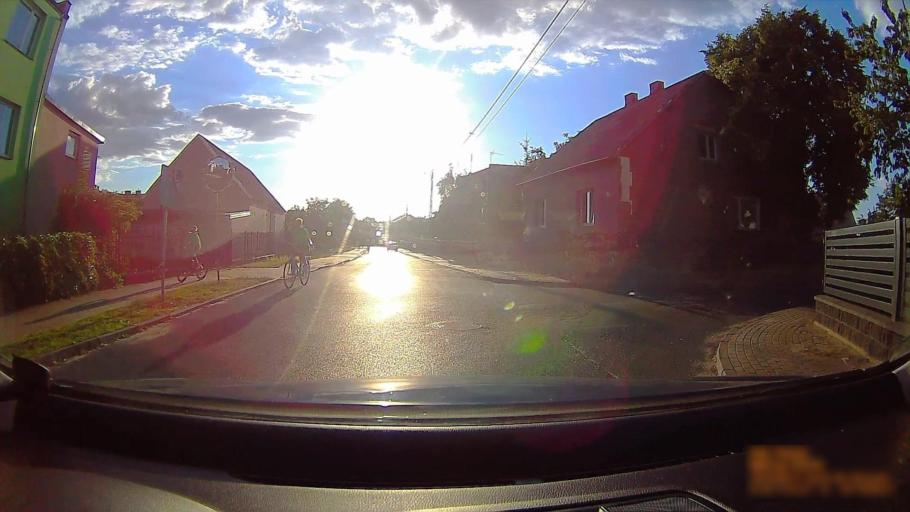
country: PL
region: Greater Poland Voivodeship
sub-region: Konin
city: Konin
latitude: 52.1919
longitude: 18.3139
